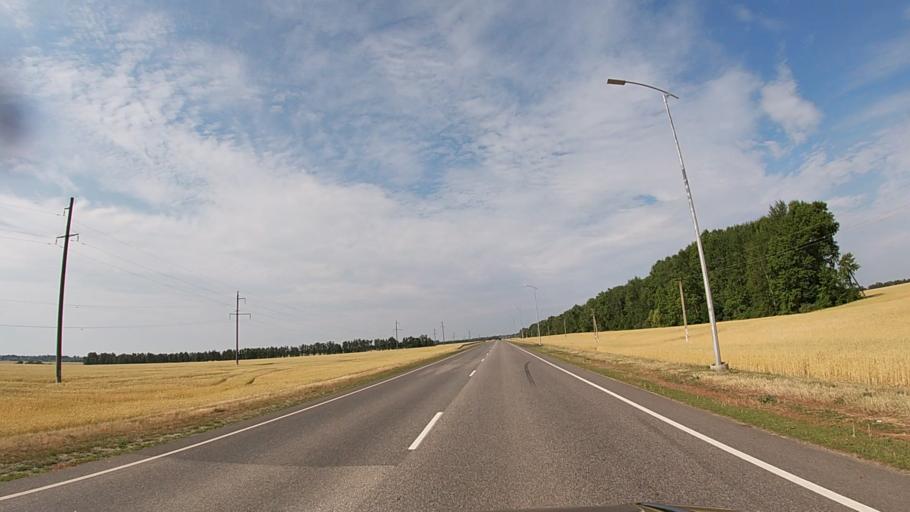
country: RU
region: Belgorod
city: Proletarskiy
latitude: 50.8176
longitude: 35.7538
